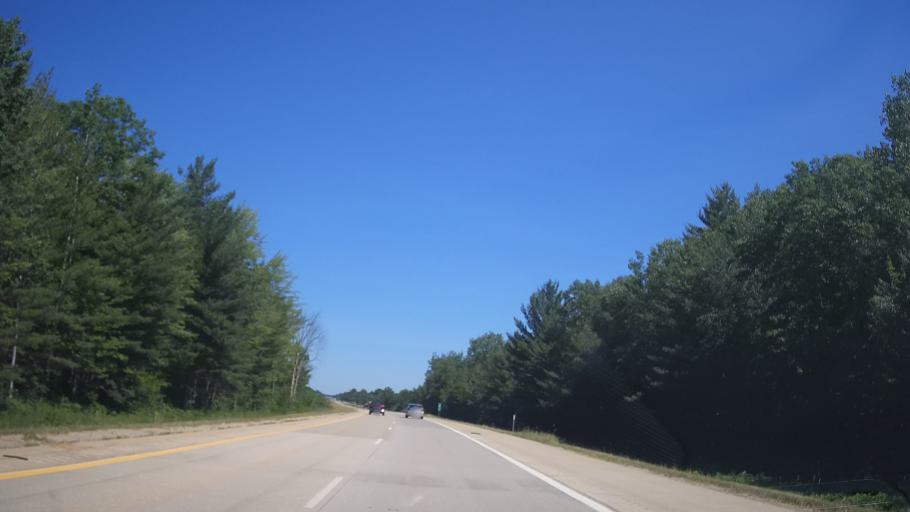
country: US
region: Michigan
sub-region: Midland County
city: Coleman
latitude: 43.7472
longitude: -84.5367
